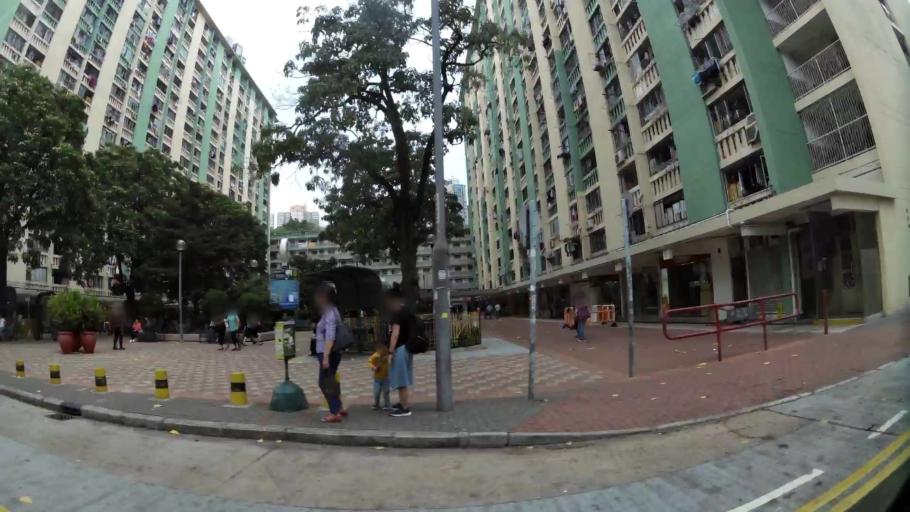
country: HK
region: Kowloon City
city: Kowloon
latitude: 22.3130
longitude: 114.1778
